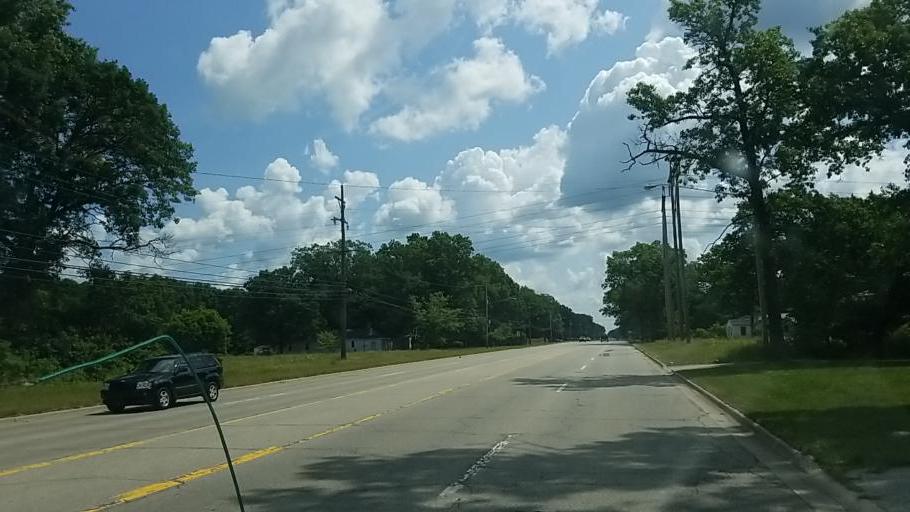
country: US
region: Michigan
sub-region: Muskegon County
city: Wolf Lake
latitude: 43.2349
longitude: -86.0836
